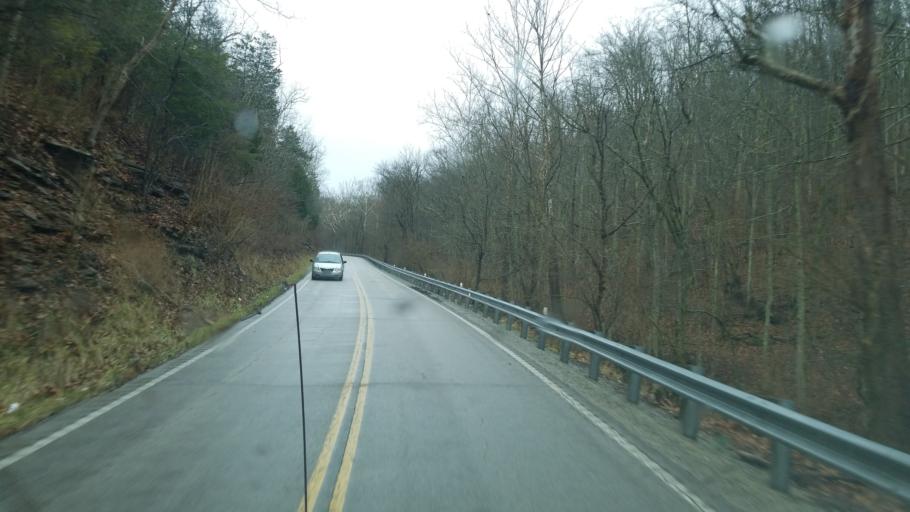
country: US
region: Kentucky
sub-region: Mason County
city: Maysville
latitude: 38.6128
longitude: -83.6936
